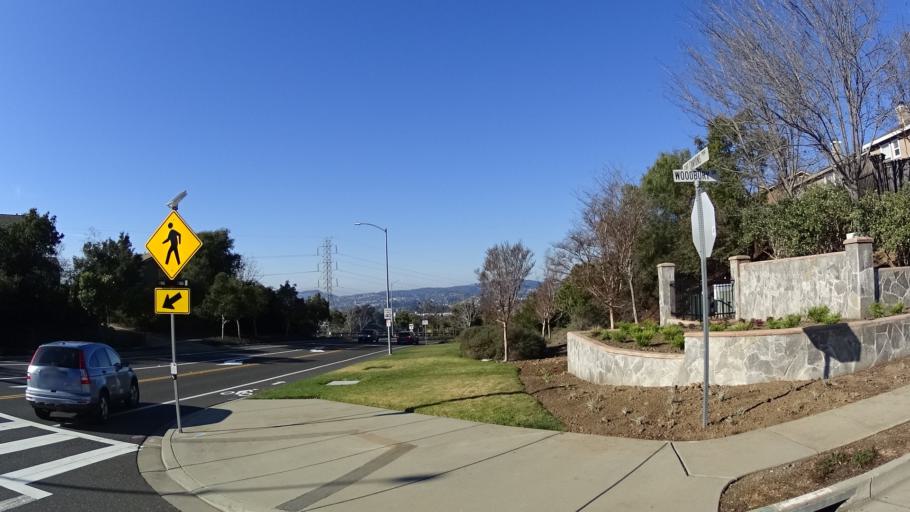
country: US
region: California
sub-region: Alameda County
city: Fairview
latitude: 37.6853
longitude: -122.0399
